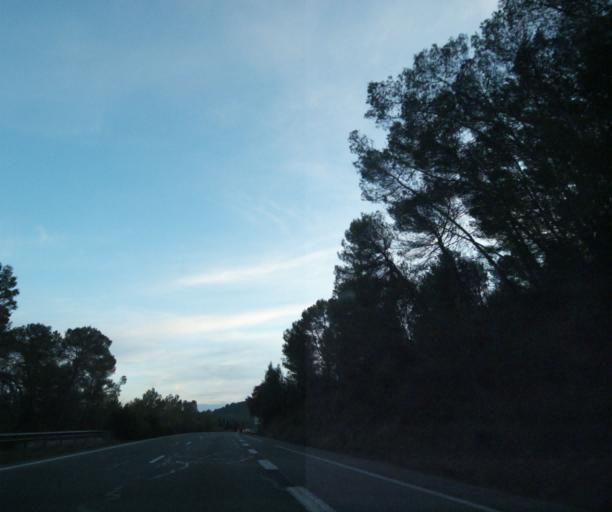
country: FR
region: Provence-Alpes-Cote d'Azur
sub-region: Departement du Var
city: Trans-en-Provence
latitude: 43.4870
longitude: 6.5083
